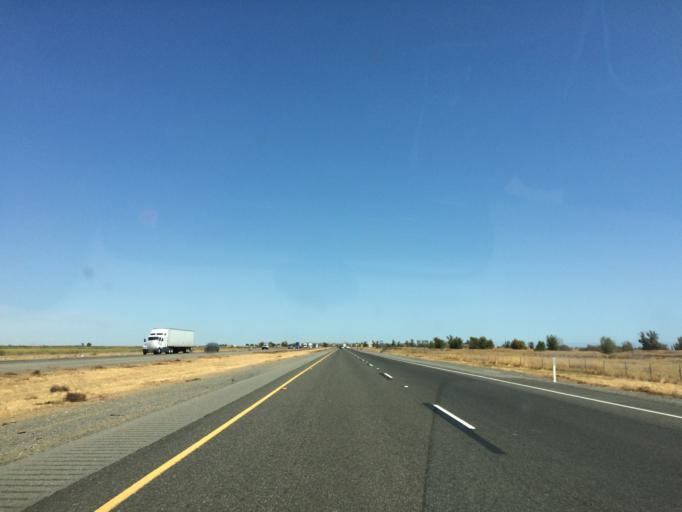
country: US
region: California
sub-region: Glenn County
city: Willows
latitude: 39.4118
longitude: -122.1949
